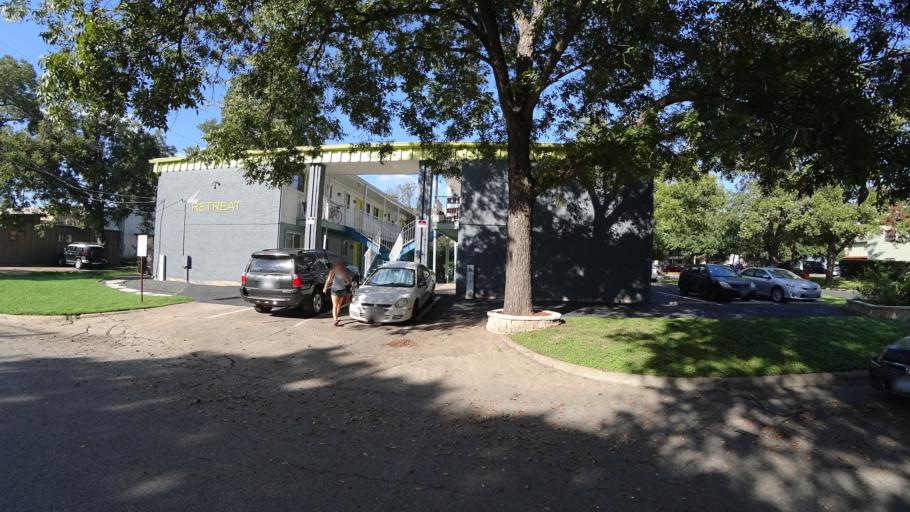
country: US
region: Texas
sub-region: Travis County
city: Austin
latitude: 30.3094
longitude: -97.7330
